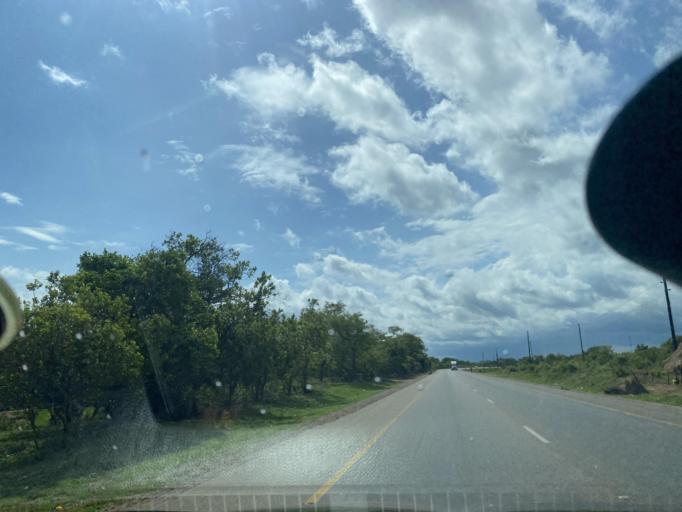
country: ZM
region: Lusaka
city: Kafue
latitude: -15.8583
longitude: 28.2638
